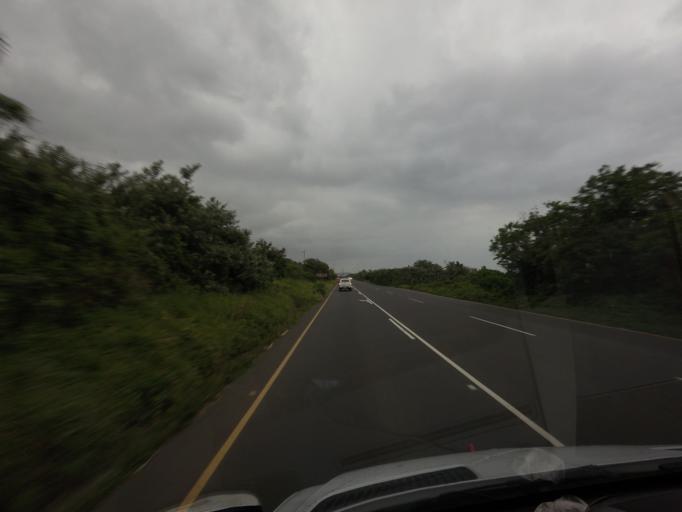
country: ZA
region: KwaZulu-Natal
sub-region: iLembe District Municipality
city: Ballitoville
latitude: -29.5997
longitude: 31.1650
